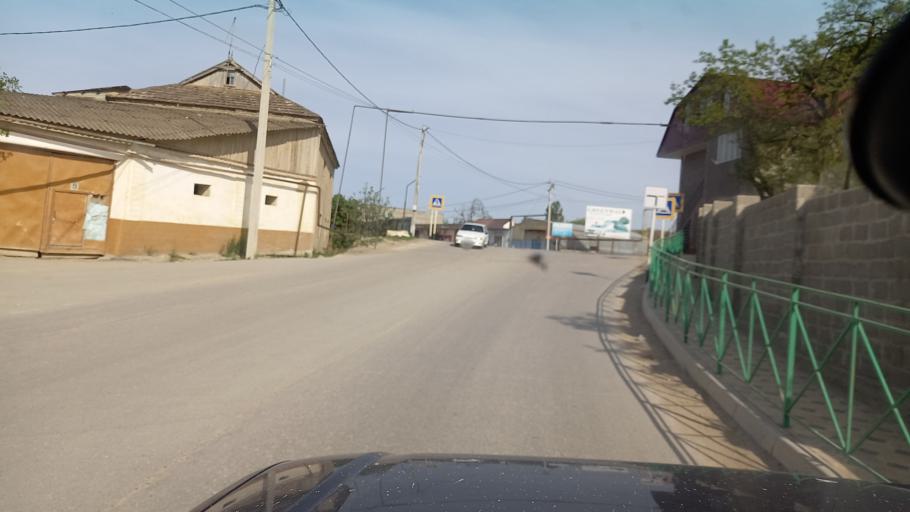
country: RU
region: Dagestan
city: Karabudakhkent
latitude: 42.7085
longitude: 47.5702
